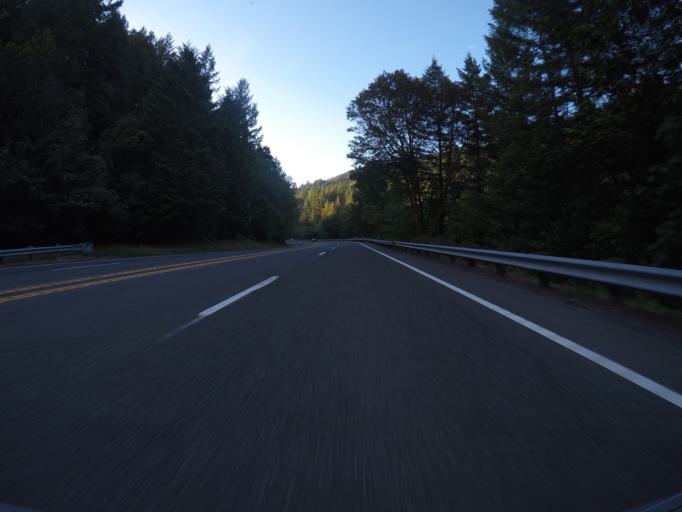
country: US
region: California
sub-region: Mendocino County
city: Laytonville
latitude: 39.5821
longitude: -123.4444
